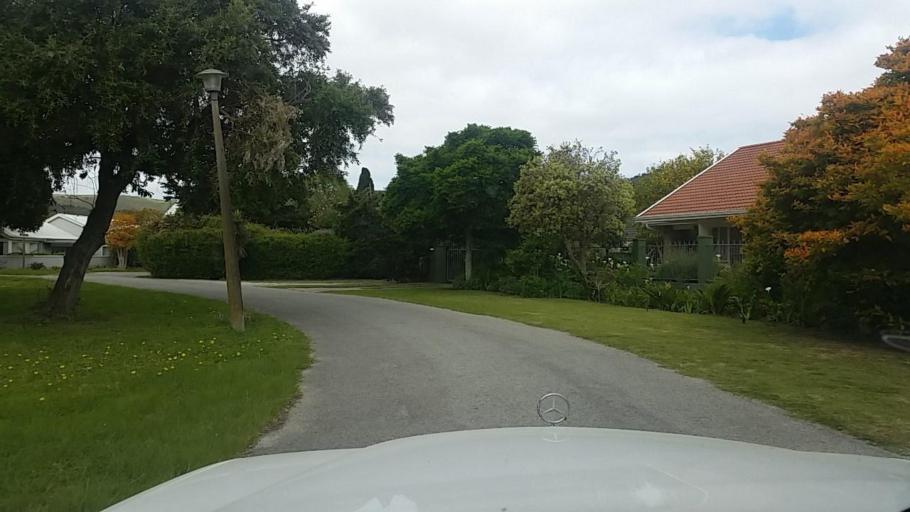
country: ZA
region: Western Cape
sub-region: Eden District Municipality
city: Knysna
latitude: -34.0678
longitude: 23.0620
